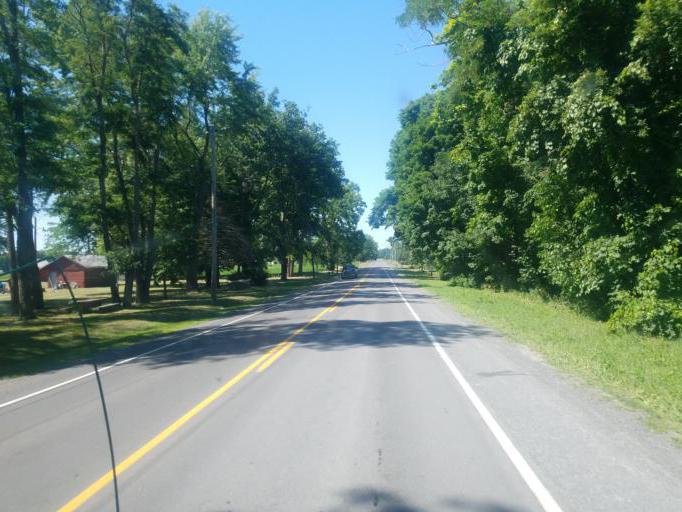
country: US
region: New York
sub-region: Ontario County
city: Phelps
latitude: 42.9372
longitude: -77.0129
